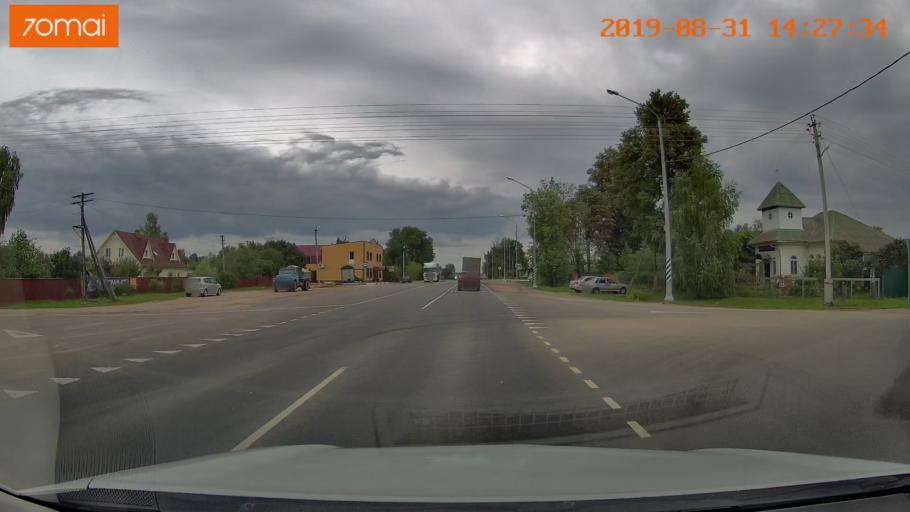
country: RU
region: Smolensk
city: Yekimovichi
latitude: 54.1168
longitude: 33.3018
